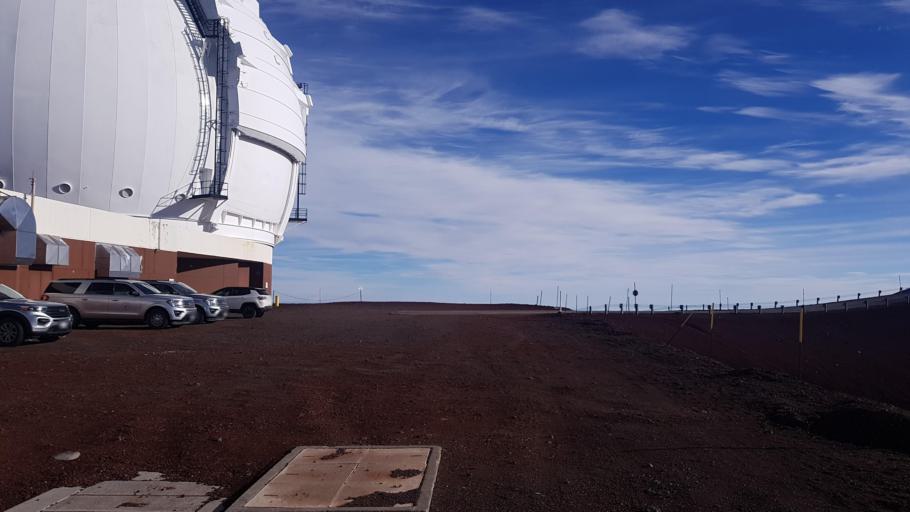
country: US
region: Hawaii
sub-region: Hawaii County
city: Honoka'a
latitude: 19.8261
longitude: -155.4743
